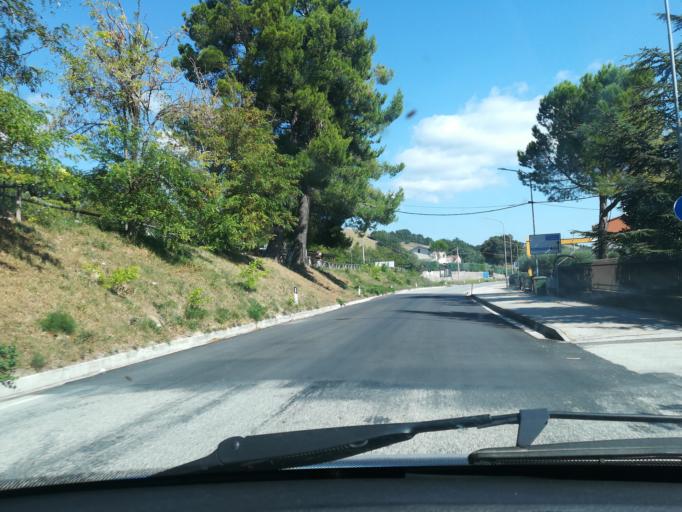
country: IT
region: The Marches
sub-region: Provincia di Macerata
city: Caldarola
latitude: 43.1483
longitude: 13.2117
